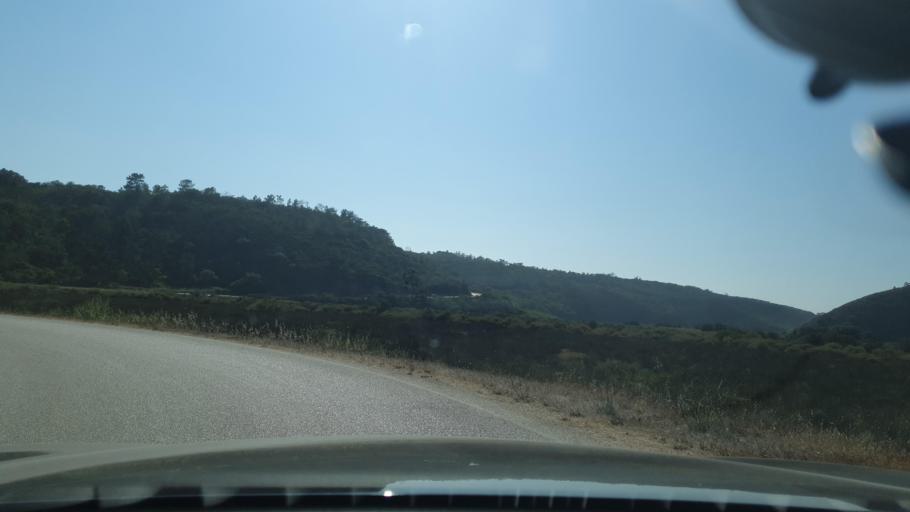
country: PT
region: Beja
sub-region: Odemira
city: Sao Teotonio
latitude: 37.4349
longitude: -8.7854
